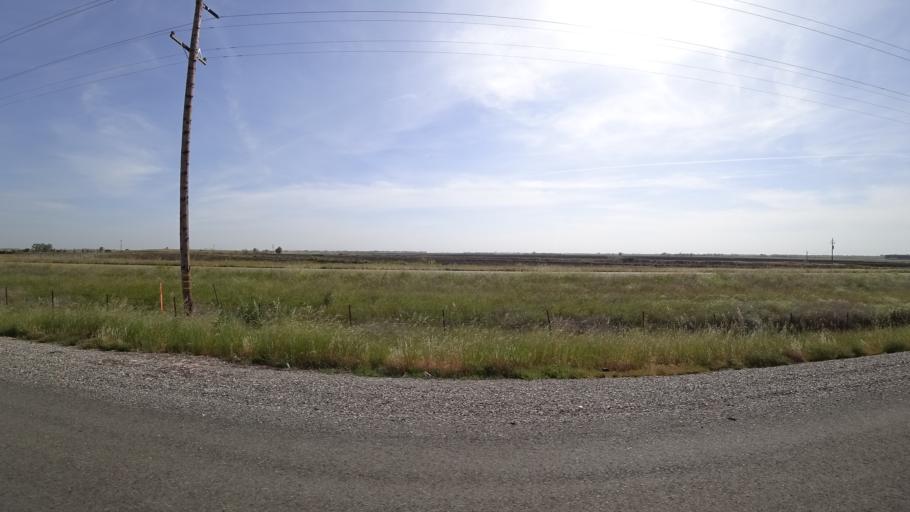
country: US
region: California
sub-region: Butte County
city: Durham
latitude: 39.6368
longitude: -121.7101
